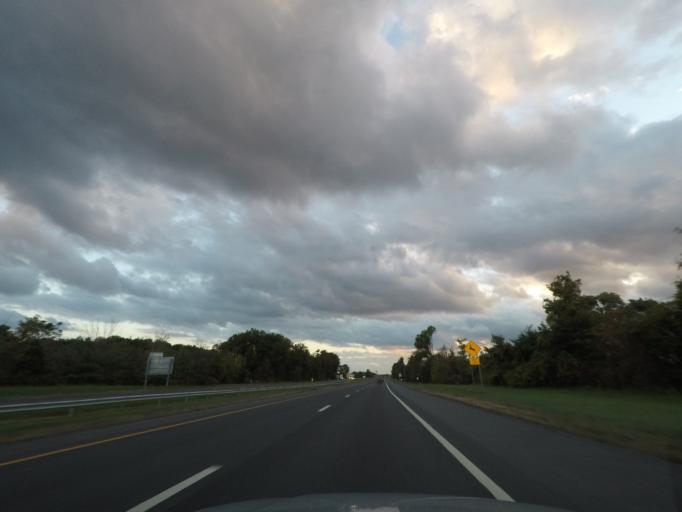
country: US
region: New York
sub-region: Ulster County
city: Saugerties
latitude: 42.0776
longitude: -73.9746
